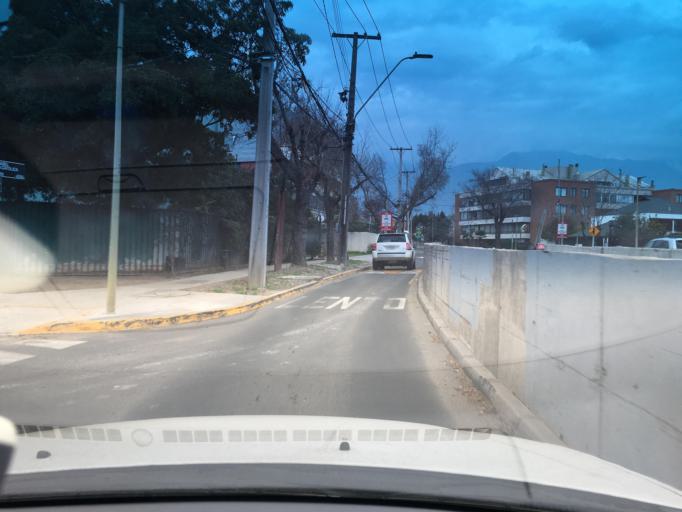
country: CL
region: Santiago Metropolitan
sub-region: Provincia de Santiago
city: Villa Presidente Frei, Nunoa, Santiago, Chile
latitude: -33.4260
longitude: -70.5749
